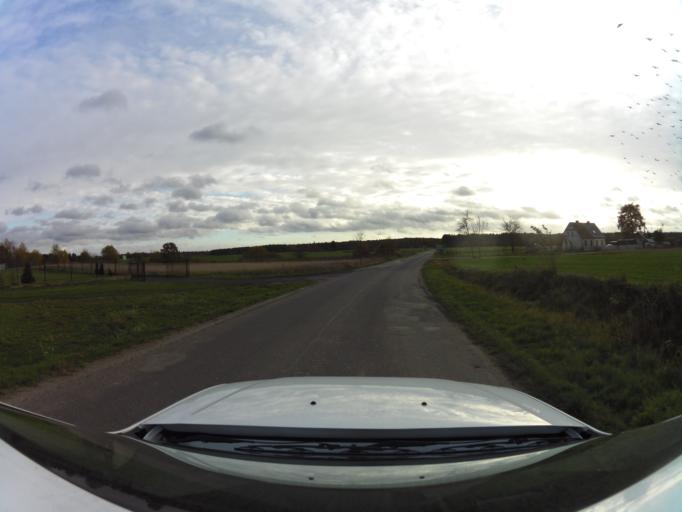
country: PL
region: West Pomeranian Voivodeship
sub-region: Powiat gryficki
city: Gryfice
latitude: 53.8144
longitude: 15.1292
